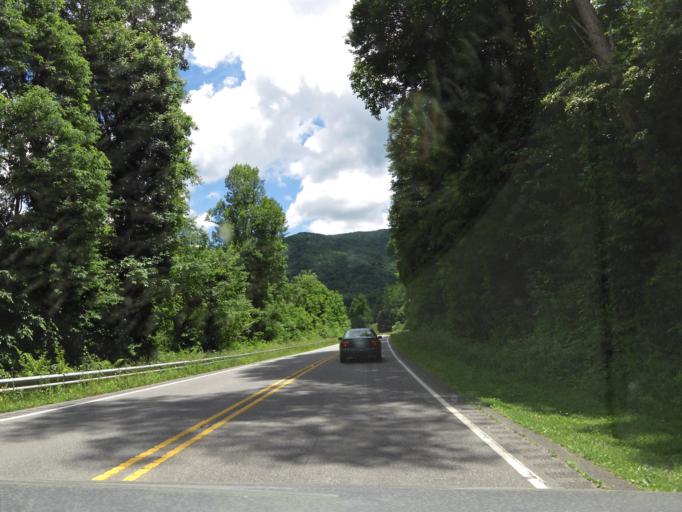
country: US
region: North Carolina
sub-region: Graham County
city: Robbinsville
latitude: 35.2720
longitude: -83.7367
